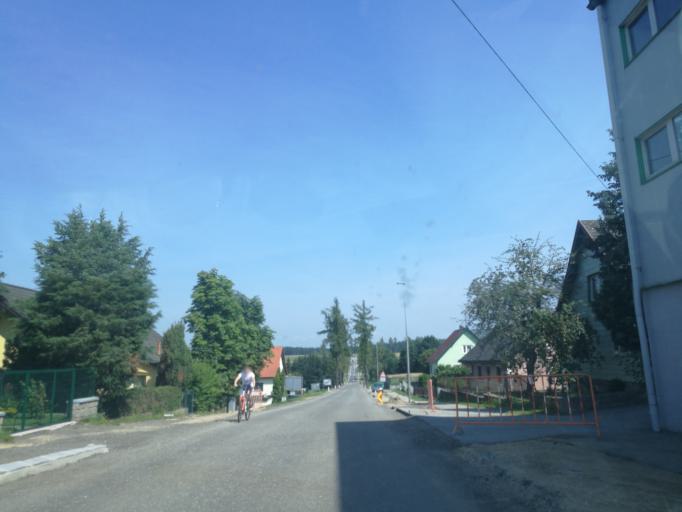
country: AT
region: Lower Austria
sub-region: Politischer Bezirk Gmund
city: Eisgarn
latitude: 48.9171
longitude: 15.1051
